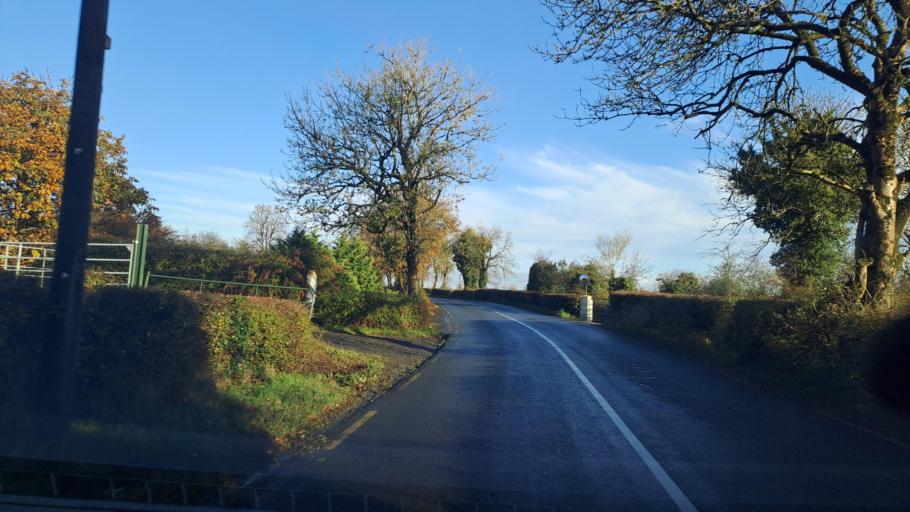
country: IE
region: Ulster
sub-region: County Monaghan
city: Monaghan
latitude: 54.1557
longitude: -7.0032
